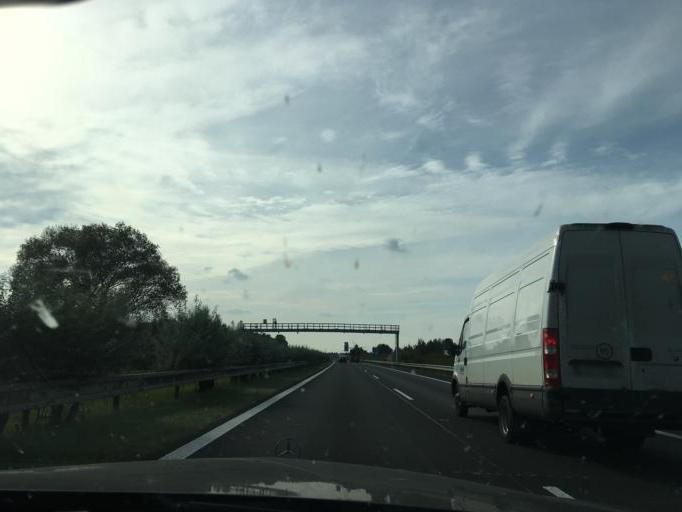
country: CZ
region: Central Bohemia
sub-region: Okres Nymburk
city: Podebrady
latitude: 50.1210
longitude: 15.0935
